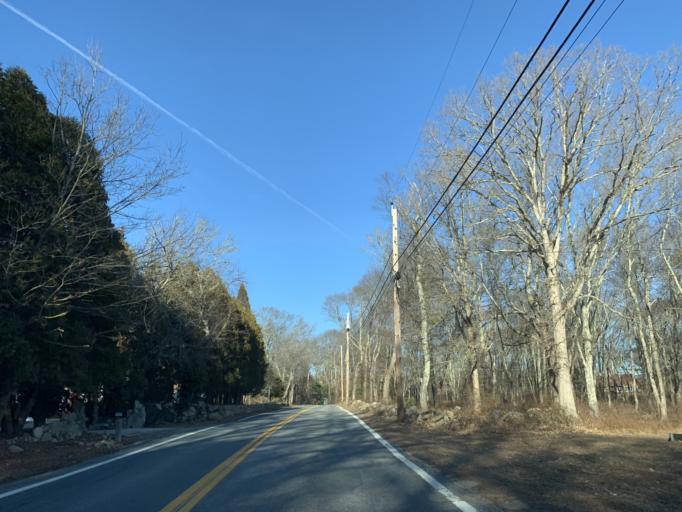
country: US
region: Rhode Island
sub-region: Washington County
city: Exeter
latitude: 41.5599
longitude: -71.5355
